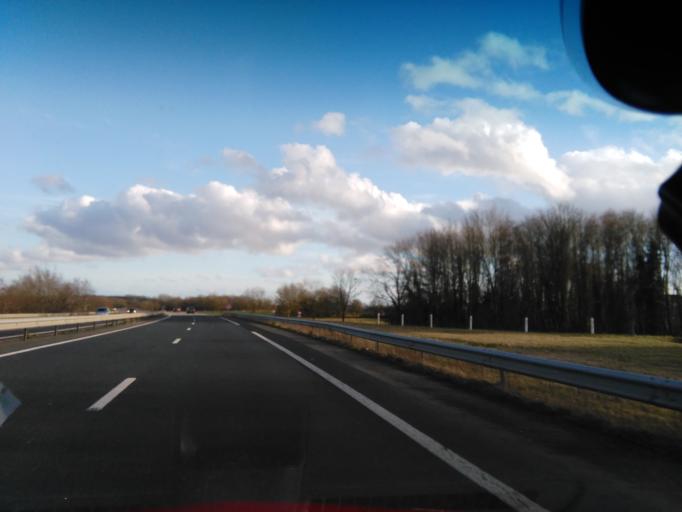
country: FR
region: Lower Normandy
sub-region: Departement du Calvados
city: Potigny
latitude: 48.9805
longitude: -0.2462
